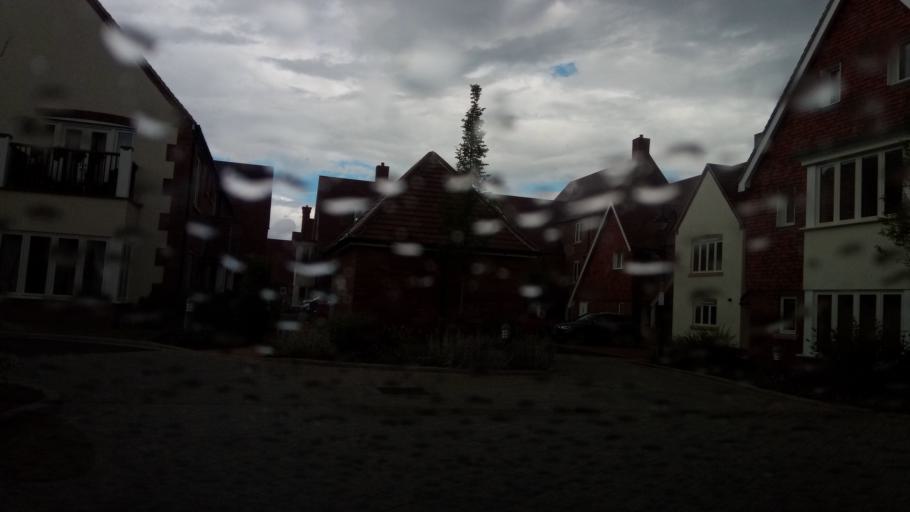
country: GB
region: England
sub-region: Leicestershire
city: Castle Donington
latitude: 52.8541
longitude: -1.3883
